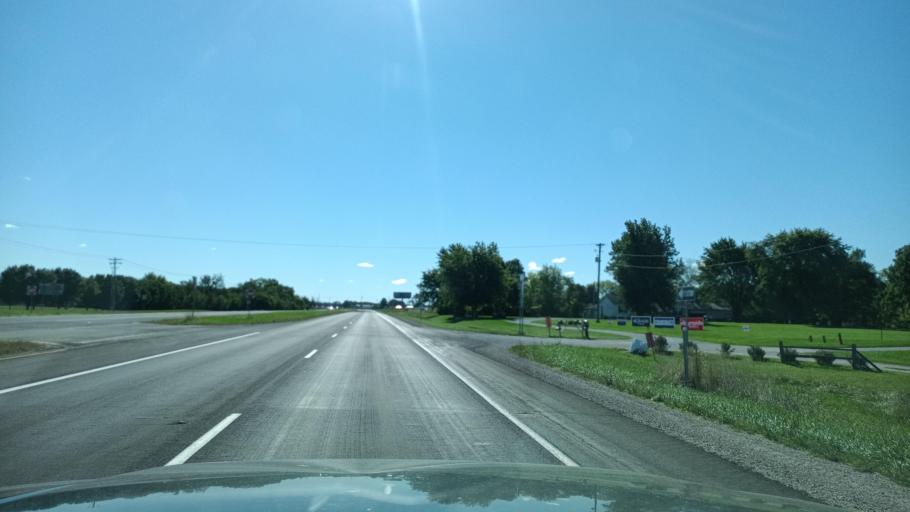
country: US
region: Iowa
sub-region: Lee County
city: Keokuk
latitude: 40.4413
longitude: -91.4339
